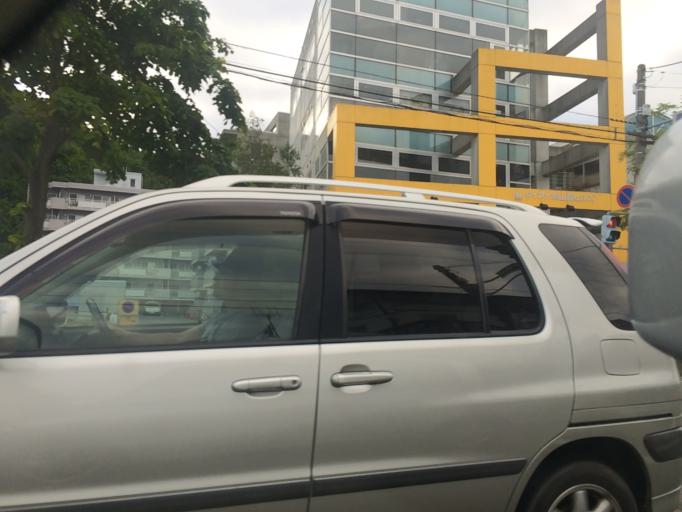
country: JP
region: Hokkaido
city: Sapporo
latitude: 43.0286
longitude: 141.3379
